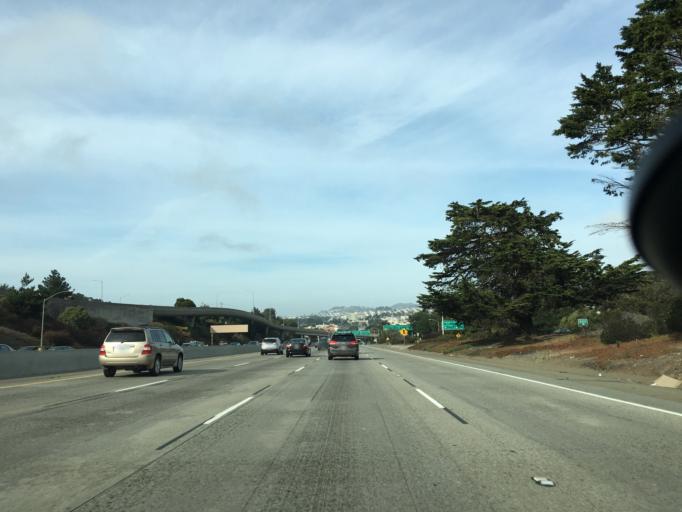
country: US
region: California
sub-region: San Mateo County
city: Colma
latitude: 37.6797
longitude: -122.4714
